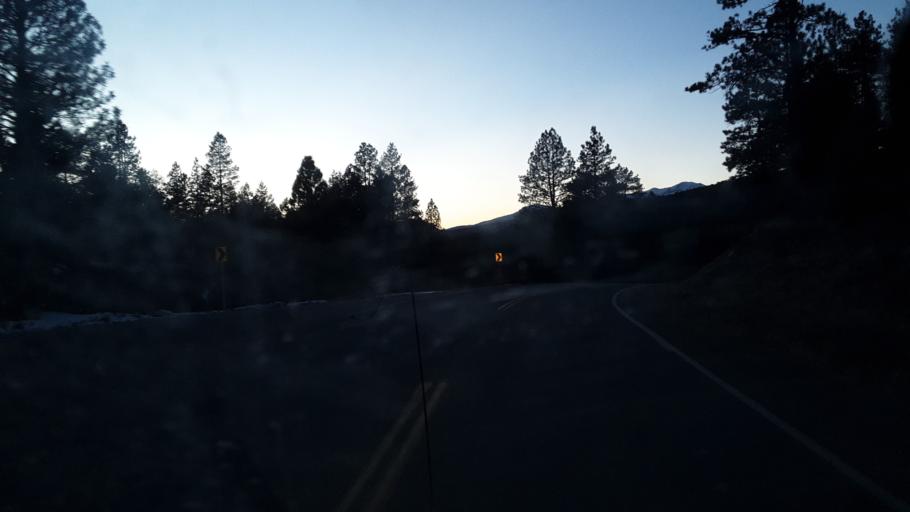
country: US
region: Colorado
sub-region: La Plata County
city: Durango
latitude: 37.3112
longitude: -107.7968
